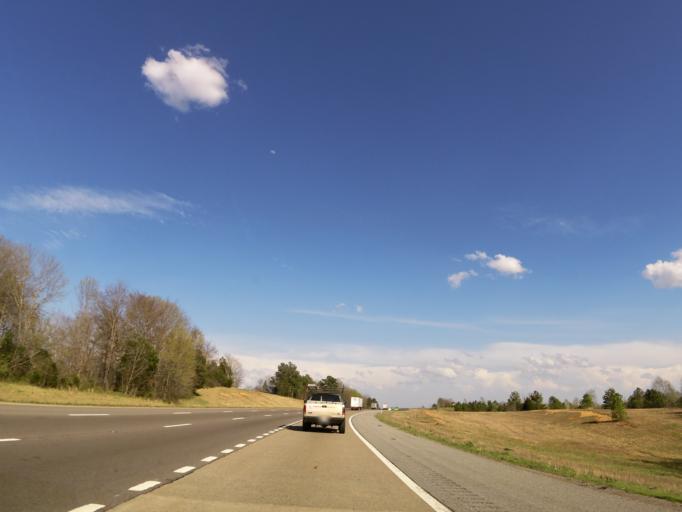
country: US
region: Tennessee
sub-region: Dickson County
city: Burns
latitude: 36.0249
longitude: -87.2778
